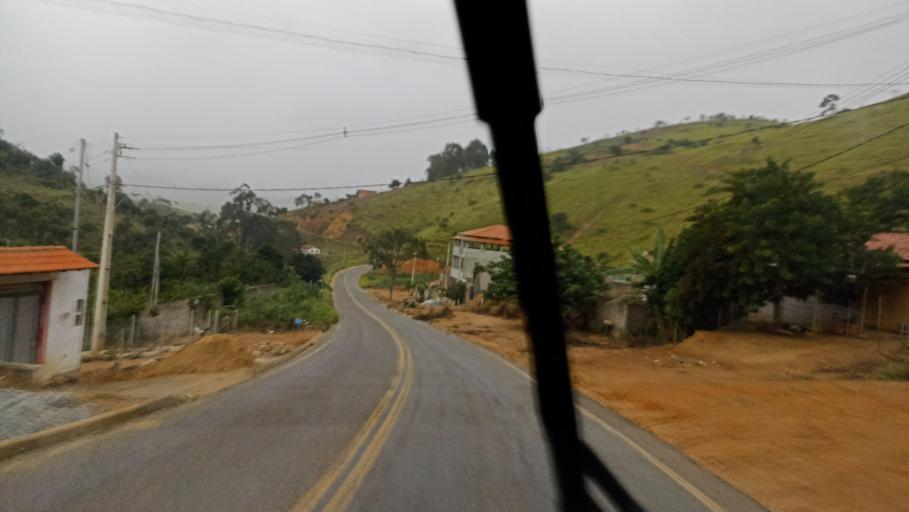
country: BR
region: Bahia
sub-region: Itanhem
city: Itanhem
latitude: -16.7350
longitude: -40.4332
